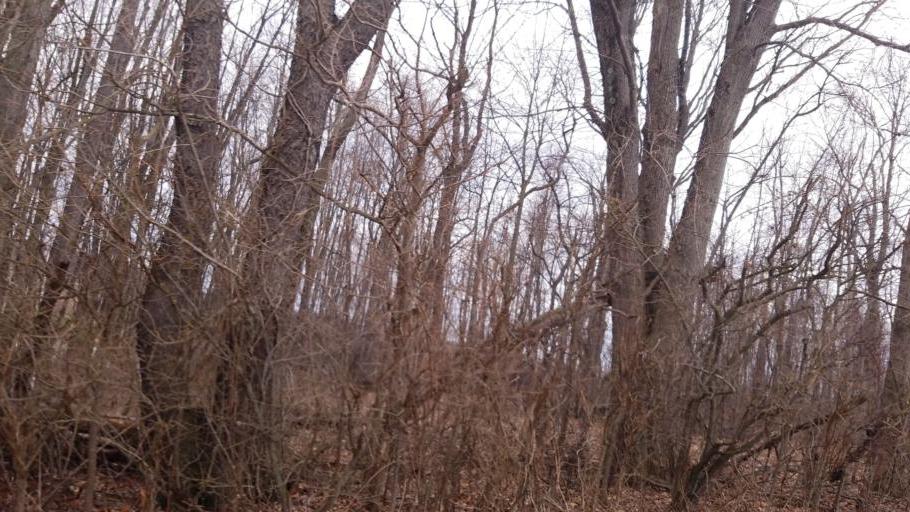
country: US
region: Ohio
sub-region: Knox County
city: Fredericktown
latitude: 40.5070
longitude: -82.4713
